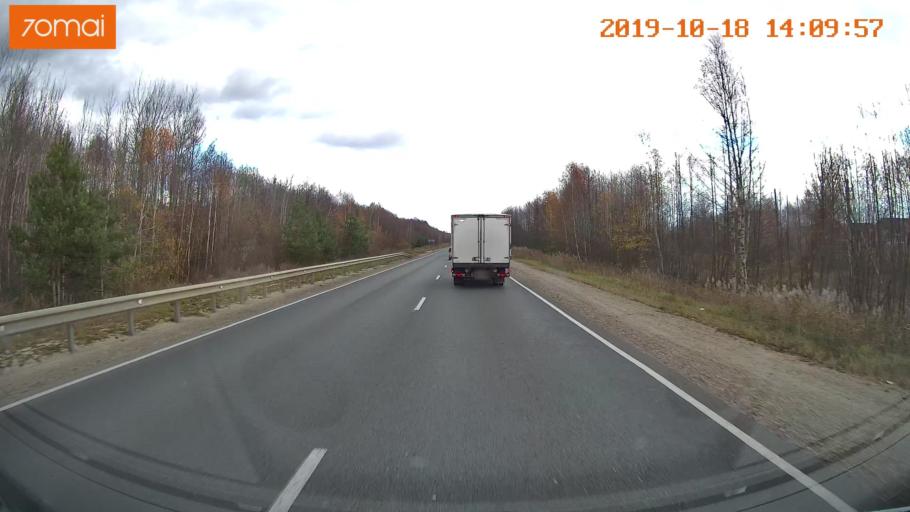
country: RU
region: Rjazan
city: Spas-Klepiki
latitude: 55.1436
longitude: 40.1956
